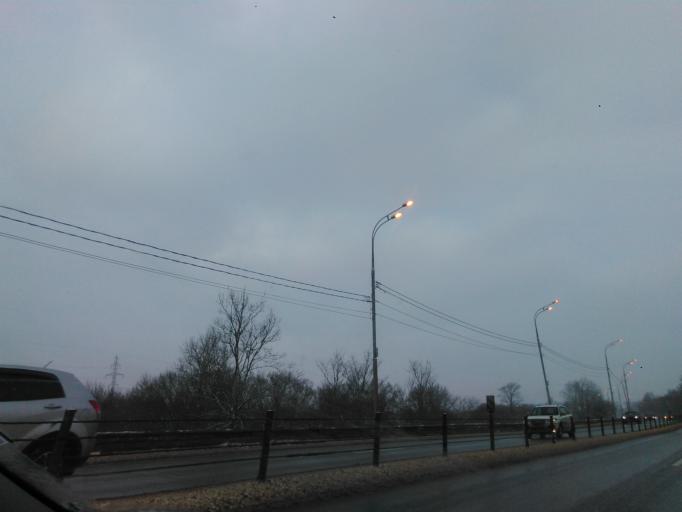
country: RU
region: Moskovskaya
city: Dedenevo
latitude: 56.2700
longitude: 37.5023
